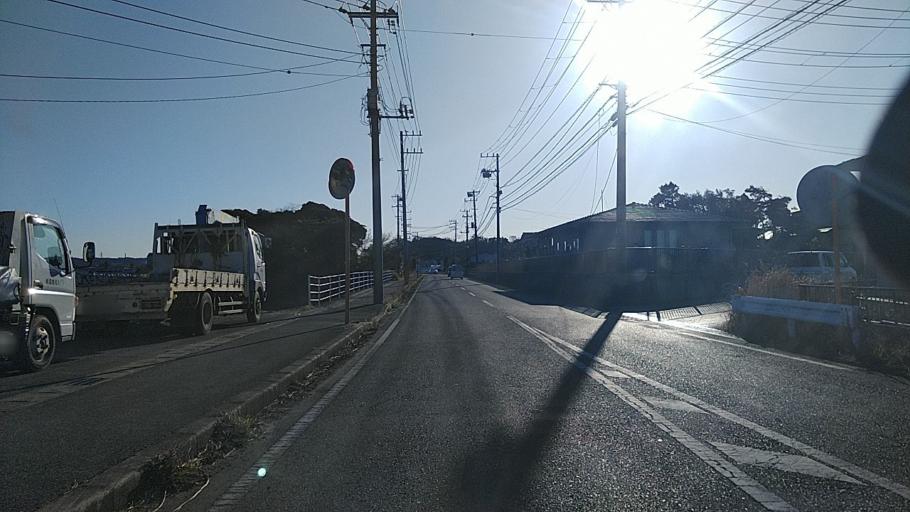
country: JP
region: Chiba
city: Kimitsu
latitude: 35.3202
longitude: 139.8842
